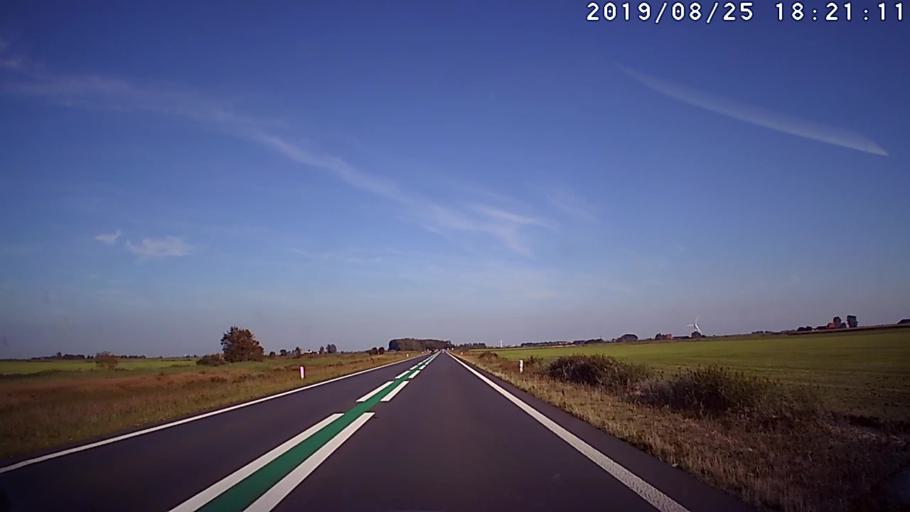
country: NL
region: Friesland
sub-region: Gemeente Gaasterlan-Sleat
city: Balk
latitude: 52.8733
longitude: 5.6268
